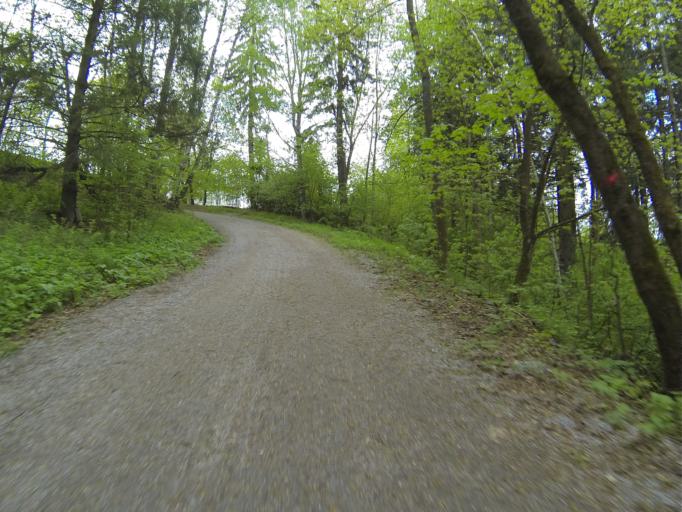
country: FI
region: Varsinais-Suomi
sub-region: Salo
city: Salo
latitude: 60.3751
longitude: 23.1247
